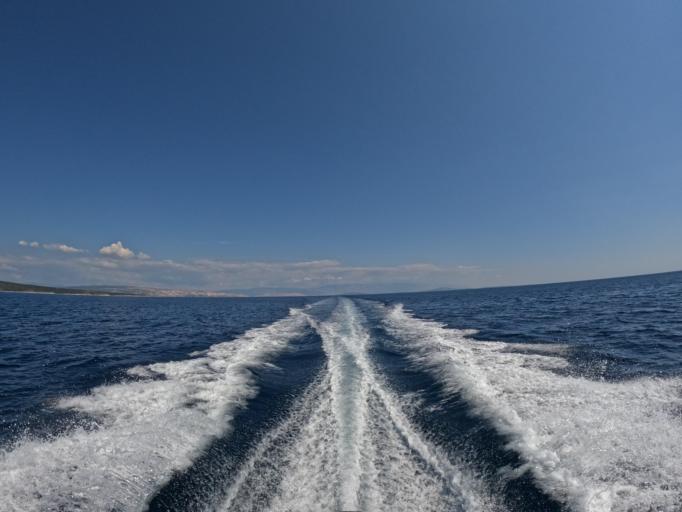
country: HR
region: Primorsko-Goranska
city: Cres
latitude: 44.9422
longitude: 14.4836
